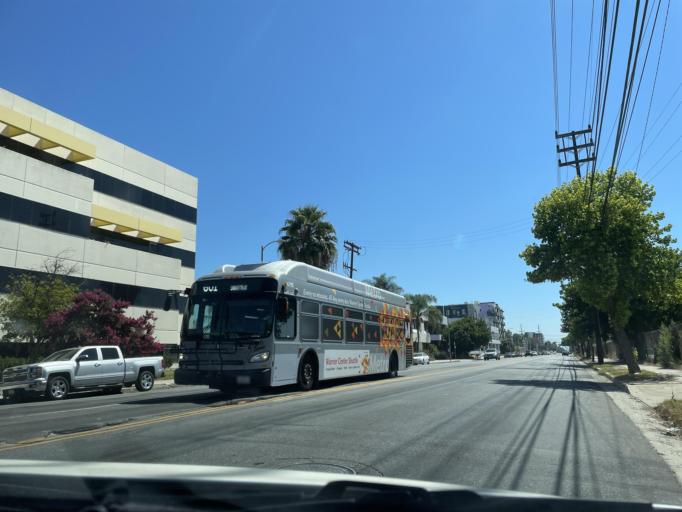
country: US
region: California
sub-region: Los Angeles County
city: Canoga Park
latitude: 34.1937
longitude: -118.6014
